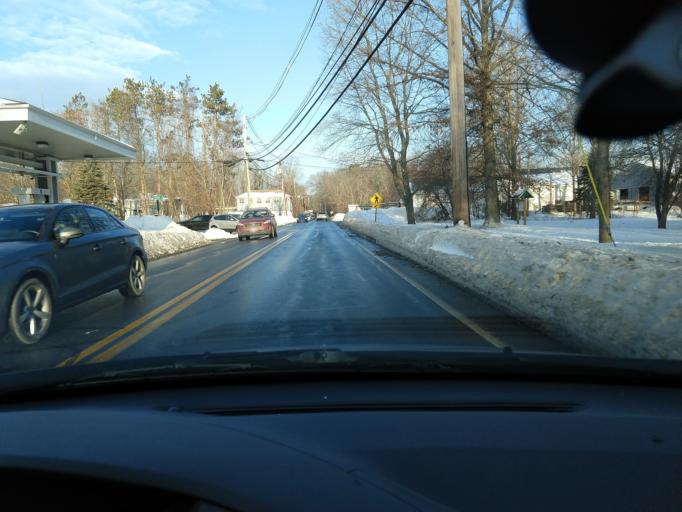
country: US
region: Massachusetts
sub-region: Middlesex County
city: Concord
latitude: 42.4636
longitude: -71.3519
